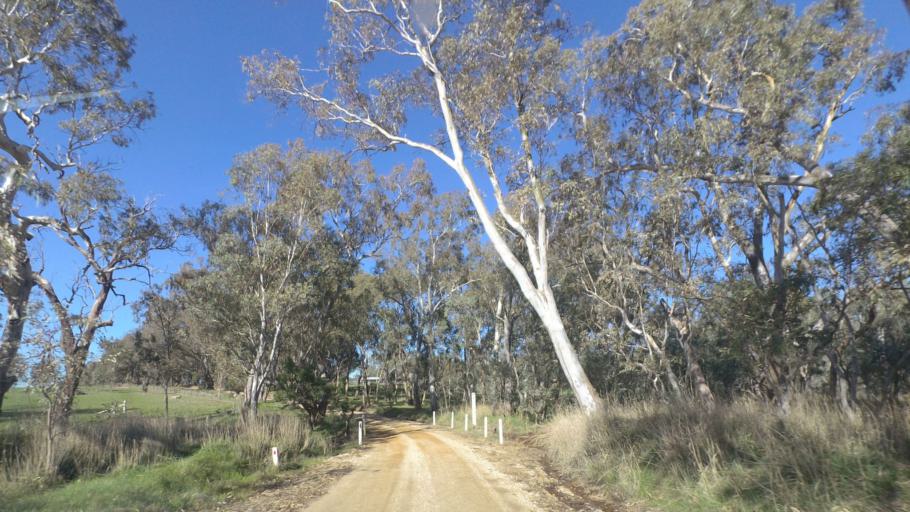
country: AU
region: Victoria
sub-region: Mount Alexander
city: Castlemaine
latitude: -36.9673
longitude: 144.3463
